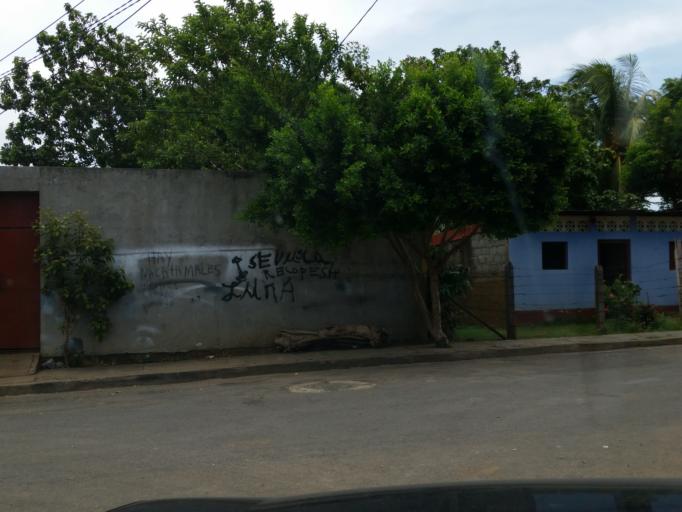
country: NI
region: Managua
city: Managua
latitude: 12.1271
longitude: -86.2813
